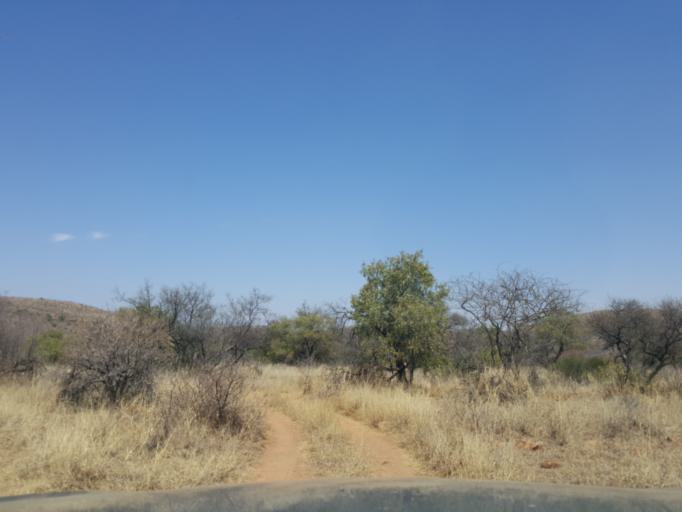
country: BW
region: South East
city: Lobatse
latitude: -25.1344
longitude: 25.6728
